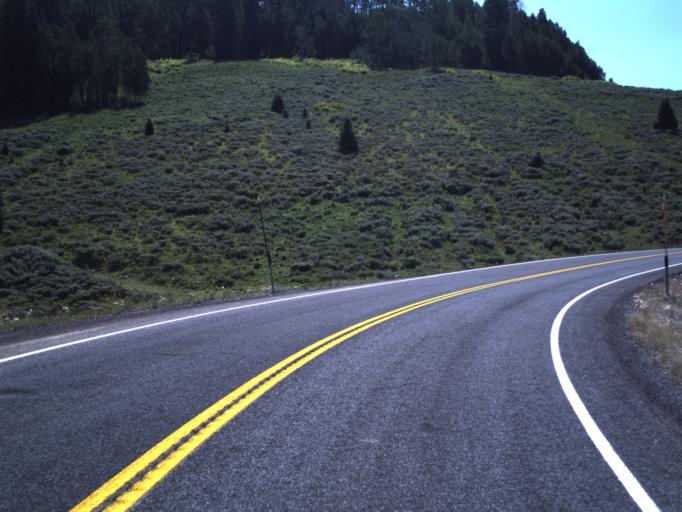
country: US
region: Utah
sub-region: Sanpete County
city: Fairview
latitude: 39.6872
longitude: -111.2451
